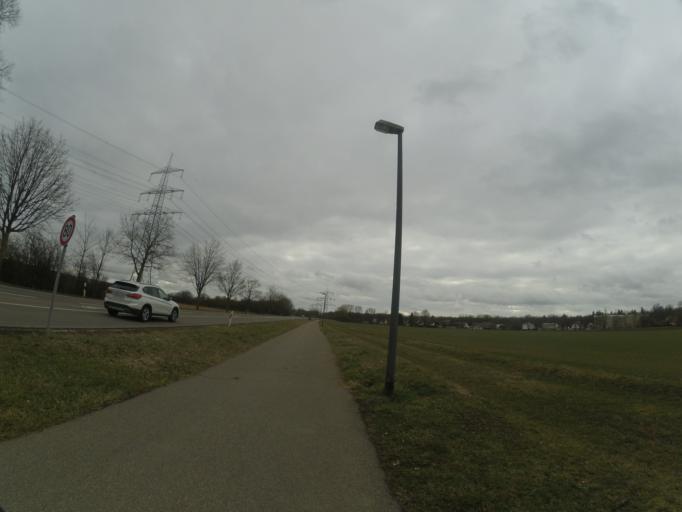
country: DE
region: Baden-Wuerttemberg
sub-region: Tuebingen Region
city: Illerrieden
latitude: 48.2987
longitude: 10.0588
